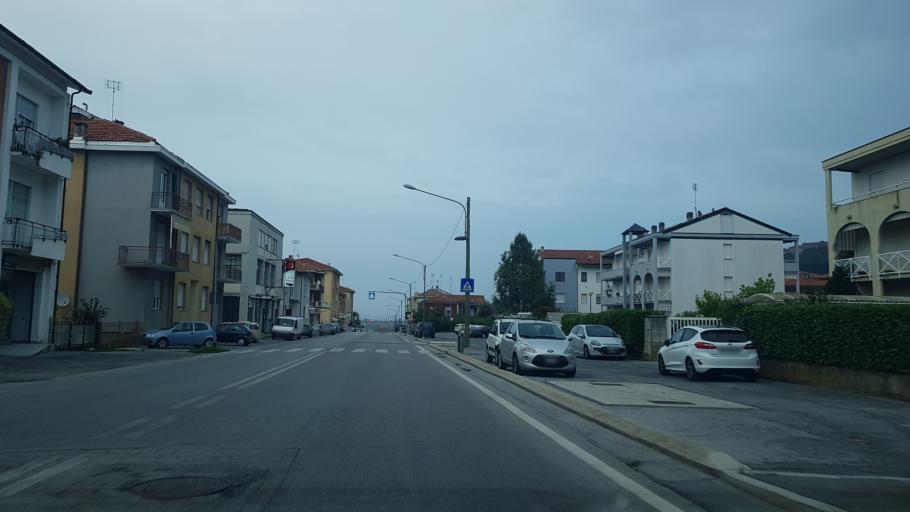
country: IT
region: Piedmont
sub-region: Provincia di Cuneo
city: Mondovi
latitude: 44.3827
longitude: 7.8141
